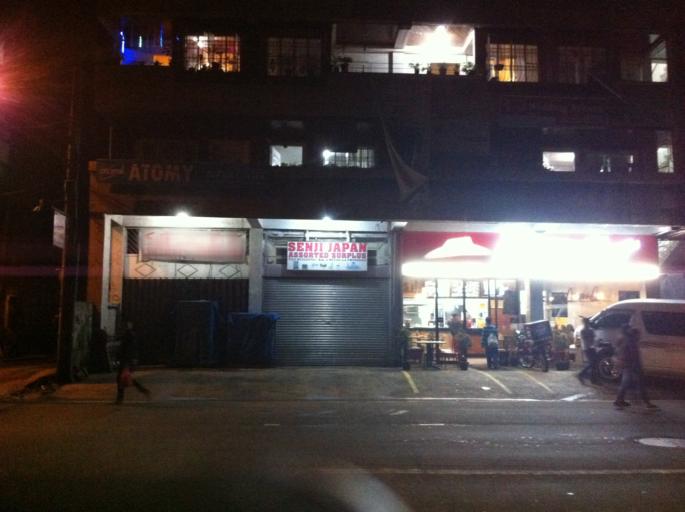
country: PH
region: Cordillera
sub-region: Province of Benguet
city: La Trinidad
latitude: 16.4544
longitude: 120.5896
